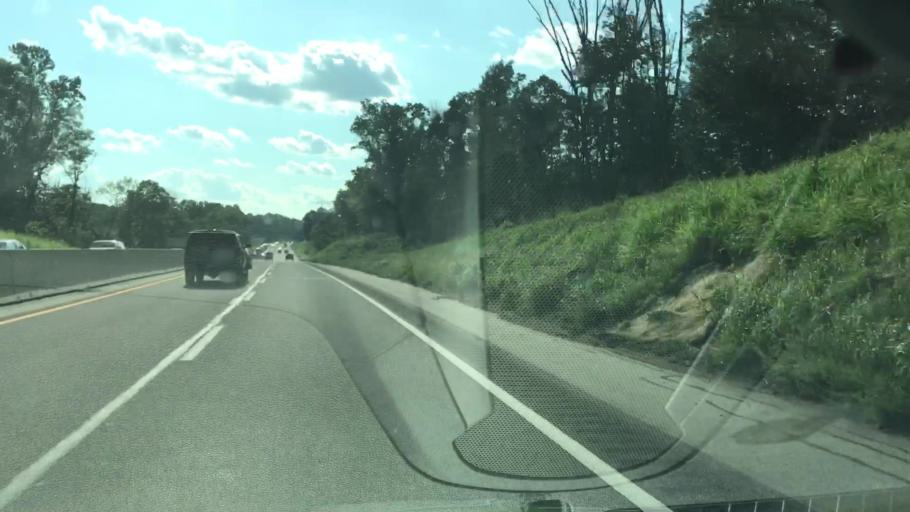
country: US
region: Pennsylvania
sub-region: Lebanon County
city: Cornwall
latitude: 40.2282
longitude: -76.4646
